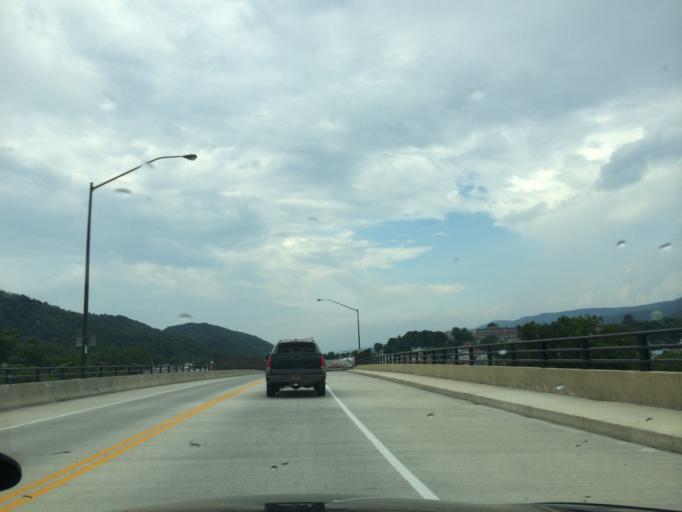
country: US
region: West Virginia
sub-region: Mineral County
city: Keyser
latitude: 39.4432
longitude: -78.9741
